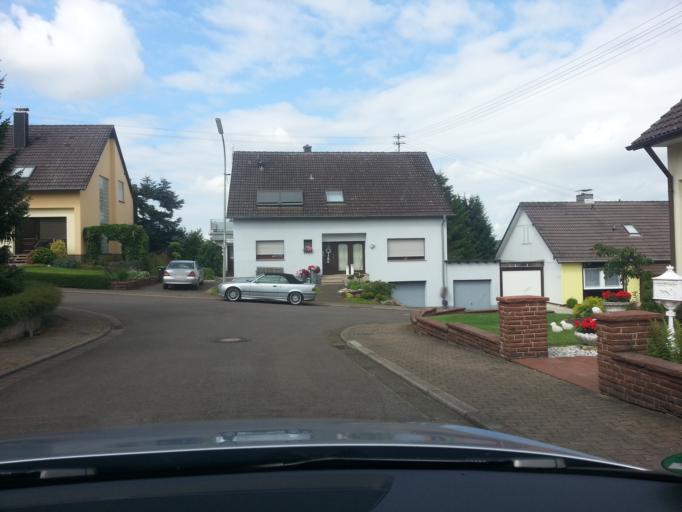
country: DE
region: Saarland
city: Weiten
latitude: 49.5275
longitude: 6.5307
